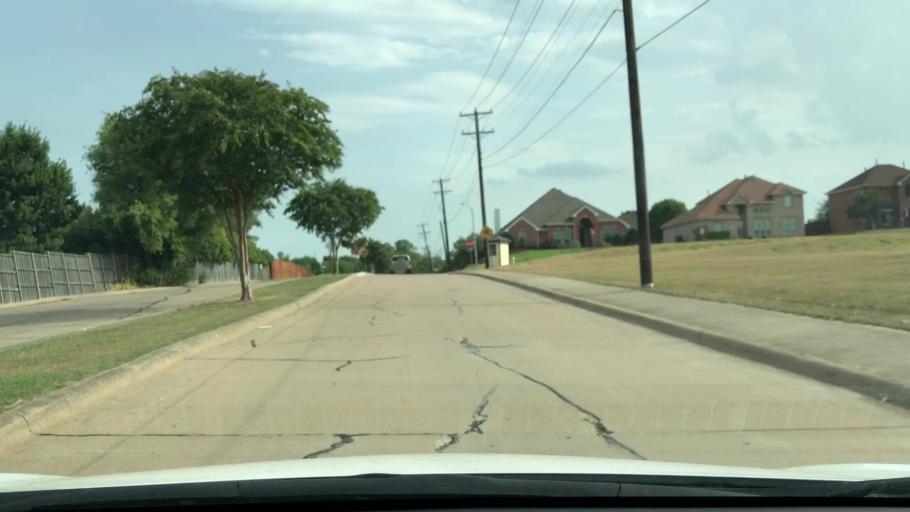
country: US
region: Texas
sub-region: Collin County
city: Wylie
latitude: 33.0098
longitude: -96.5215
